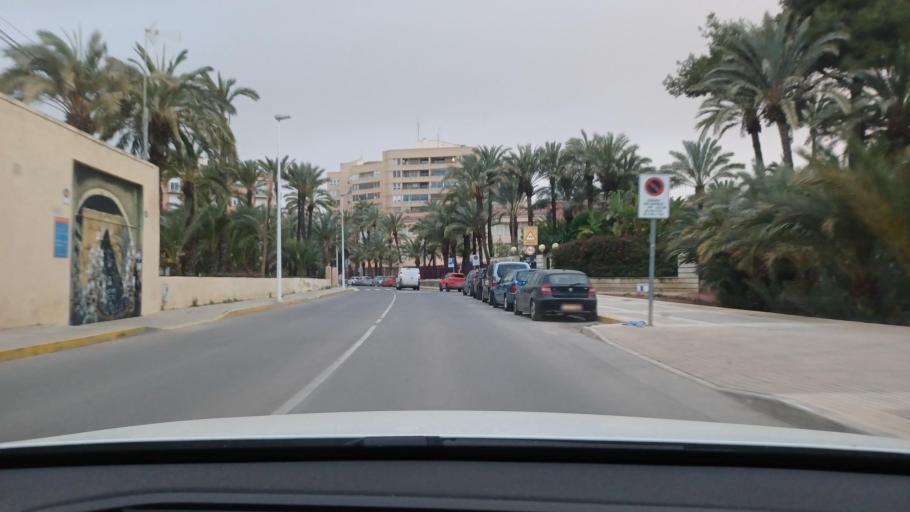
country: ES
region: Valencia
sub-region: Provincia de Alicante
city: Elche
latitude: 38.2609
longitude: -0.6933
